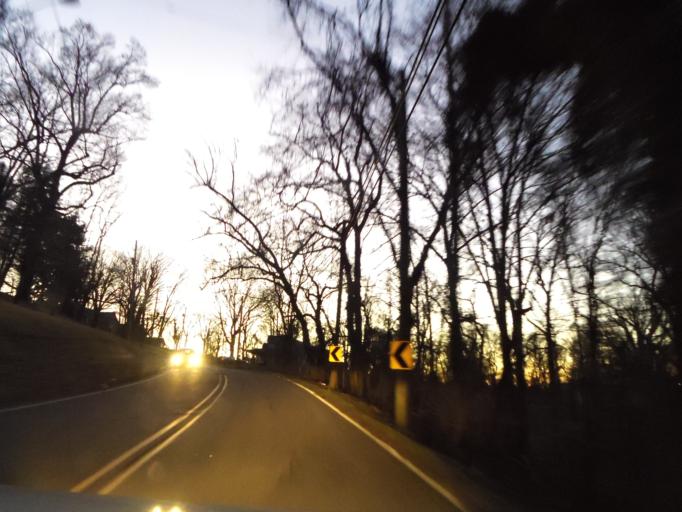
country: US
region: Tennessee
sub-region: Knox County
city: Knoxville
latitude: 35.9564
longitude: -83.8711
